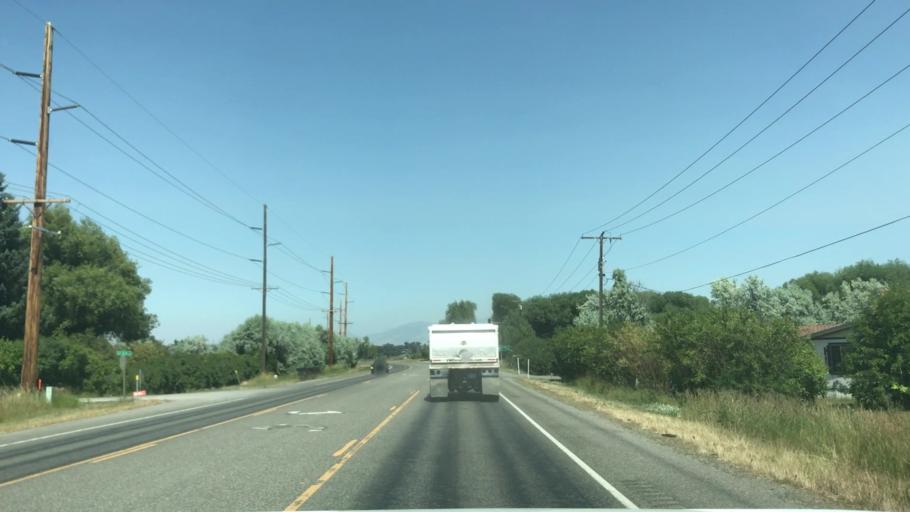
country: US
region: Montana
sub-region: Gallatin County
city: Four Corners
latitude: 45.6562
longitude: -111.1873
